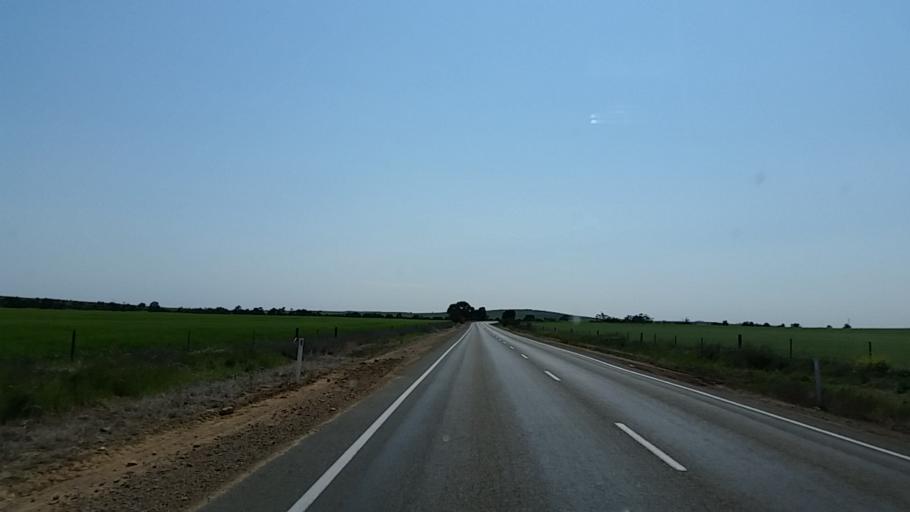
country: AU
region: South Australia
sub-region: Northern Areas
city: Jamestown
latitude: -33.2311
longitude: 138.3929
